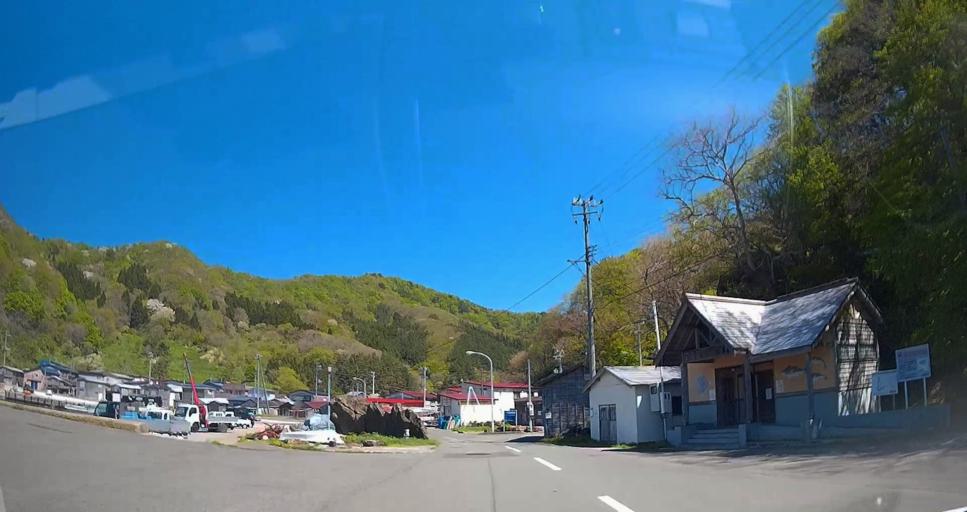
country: JP
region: Aomori
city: Aomori Shi
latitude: 41.1414
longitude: 140.7740
